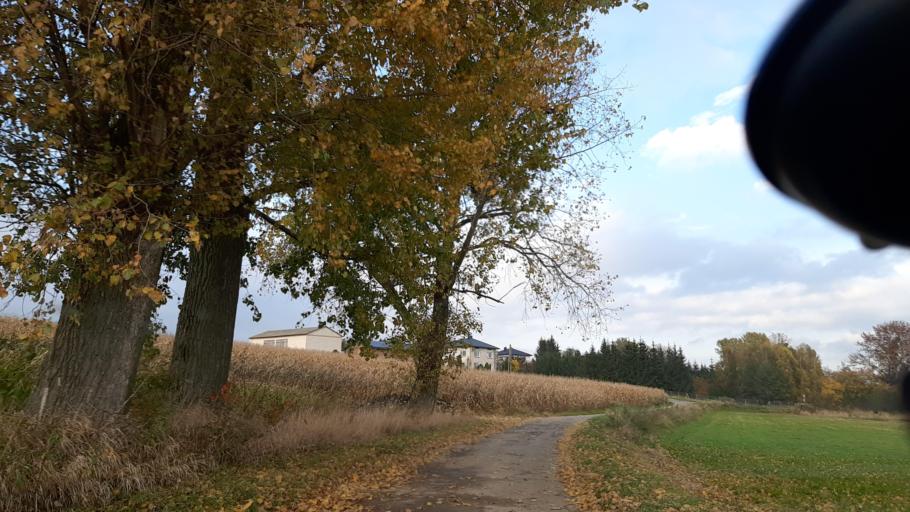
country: PL
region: Lublin Voivodeship
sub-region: Powiat lubelski
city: Garbow
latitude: 51.3351
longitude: 22.2857
